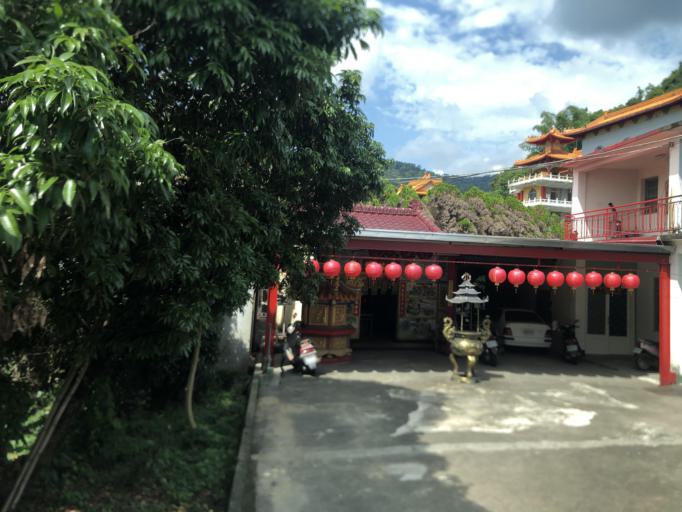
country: TW
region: Taiwan
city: Yujing
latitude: 22.9328
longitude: 120.5882
